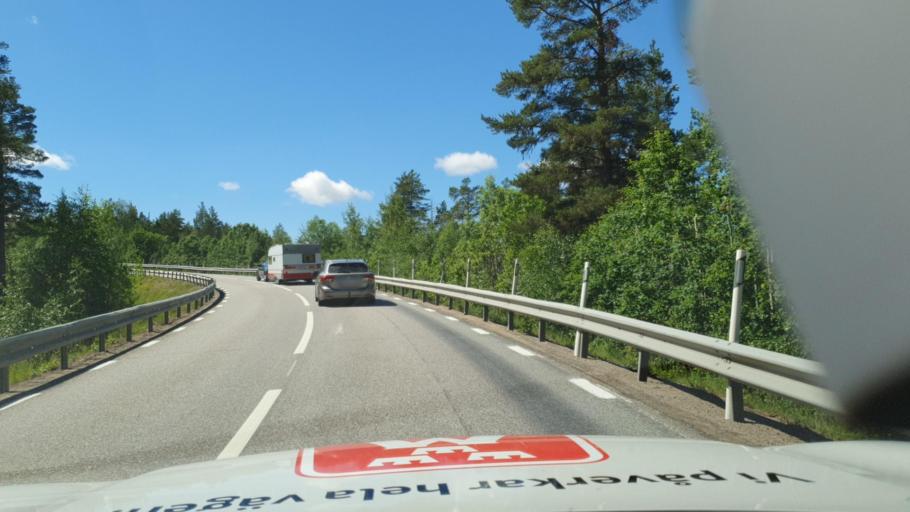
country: SE
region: Jaemtland
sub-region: Harjedalens Kommun
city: Sveg
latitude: 62.0298
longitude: 14.4096
